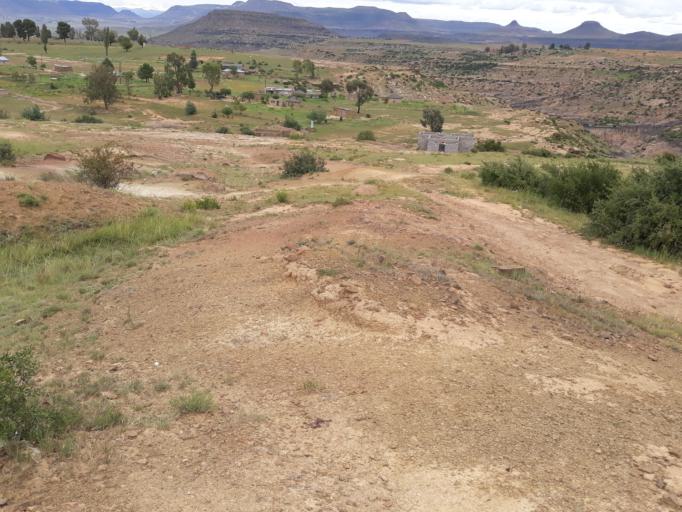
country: LS
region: Quthing
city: Quthing
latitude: -30.3342
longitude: 27.5319
